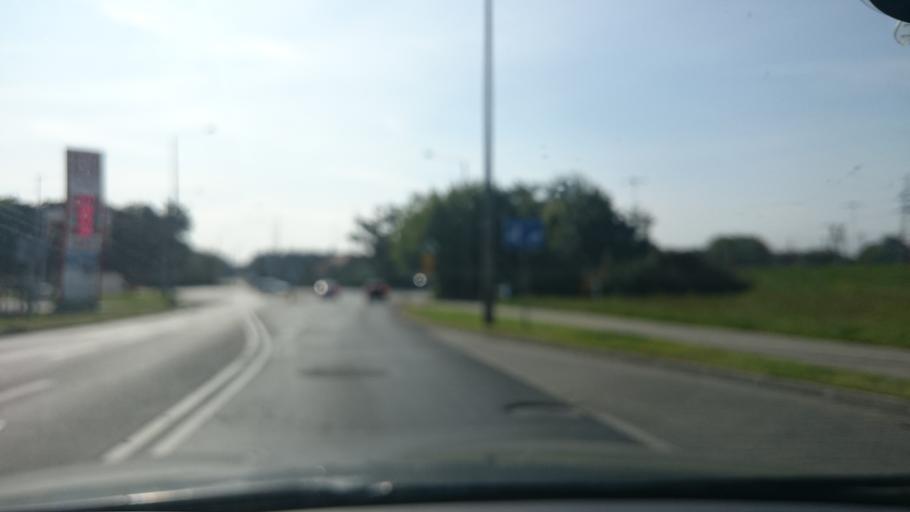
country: PL
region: Kujawsko-Pomorskie
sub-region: Grudziadz
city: Grudziadz
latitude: 53.4531
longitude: 18.7314
